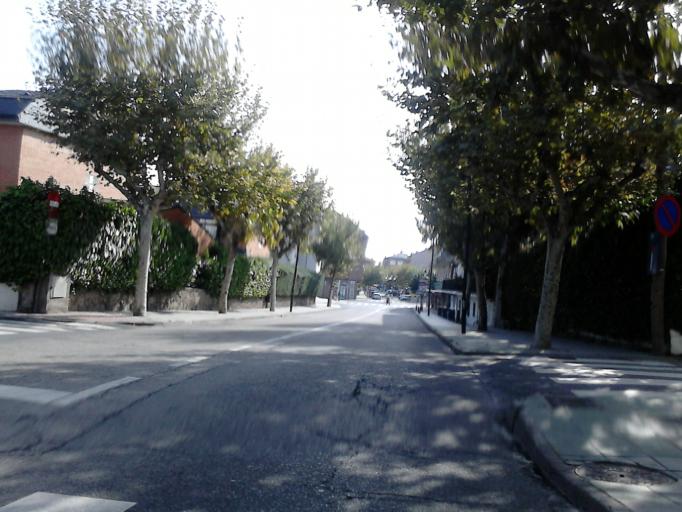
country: ES
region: Madrid
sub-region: Provincia de Madrid
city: Galapagar
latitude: 40.5807
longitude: -4.0074
